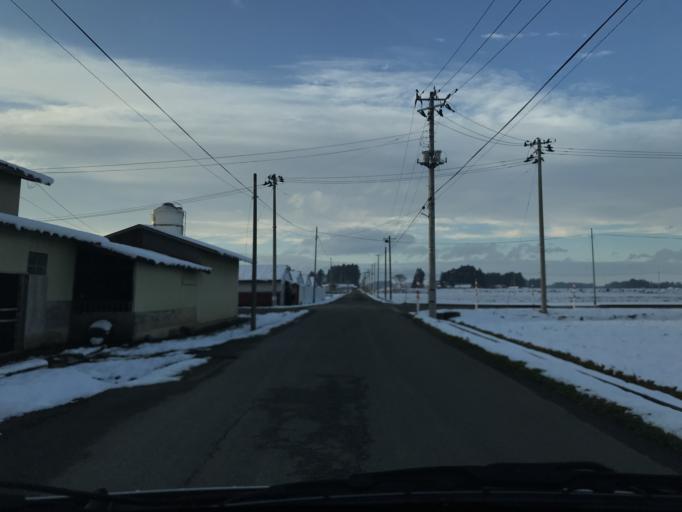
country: JP
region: Iwate
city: Mizusawa
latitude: 39.0527
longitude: 141.0977
